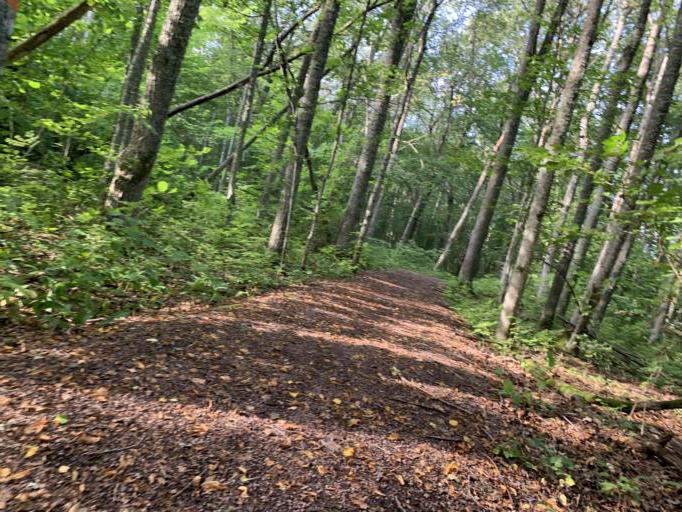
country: SE
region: Vaestmanland
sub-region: Hallstahammars Kommun
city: Kolback
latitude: 59.4792
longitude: 16.2125
